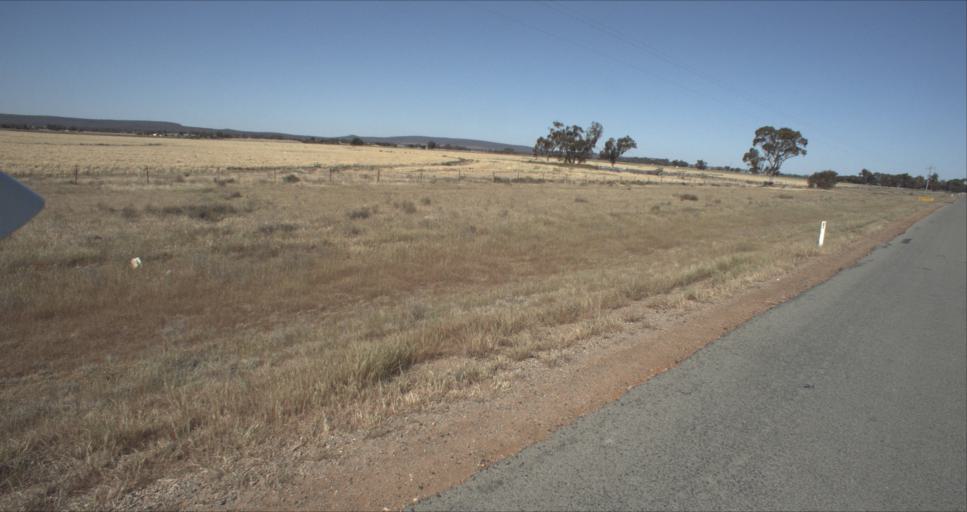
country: AU
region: New South Wales
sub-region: Leeton
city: Leeton
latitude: -34.4957
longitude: 146.3888
